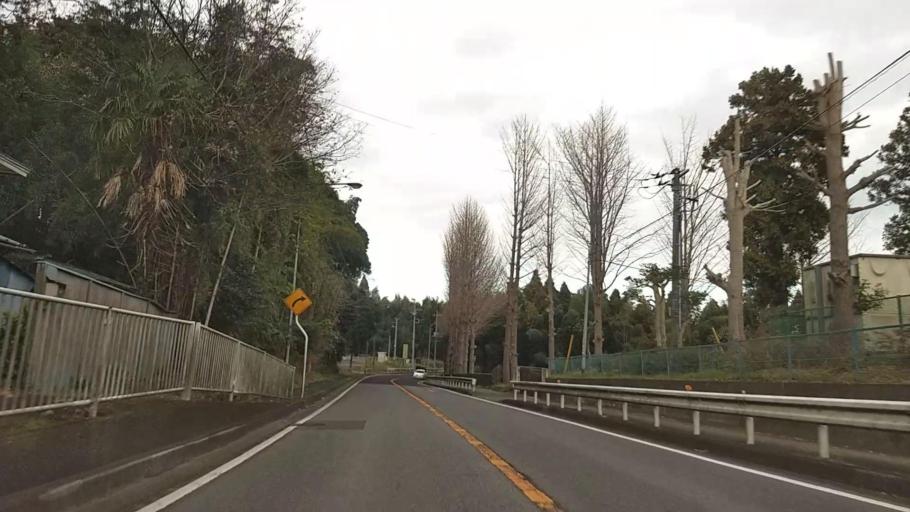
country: JP
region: Chiba
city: Yotsukaido
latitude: 35.5871
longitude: 140.2247
